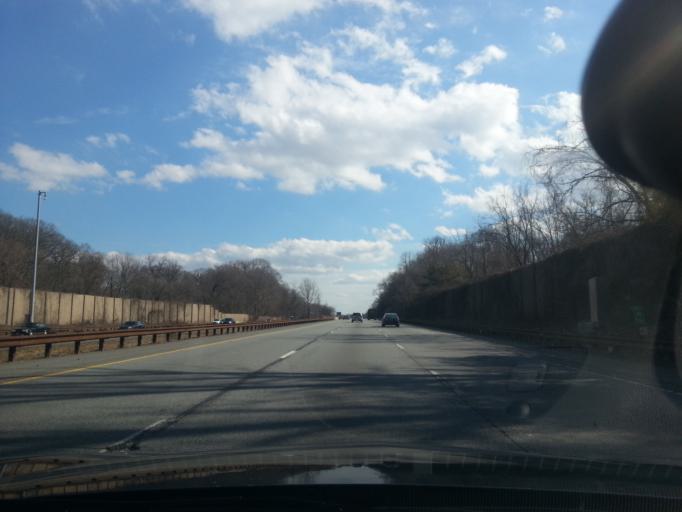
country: US
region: Pennsylvania
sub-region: Delaware County
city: Radnor
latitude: 40.0163
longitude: -75.3581
